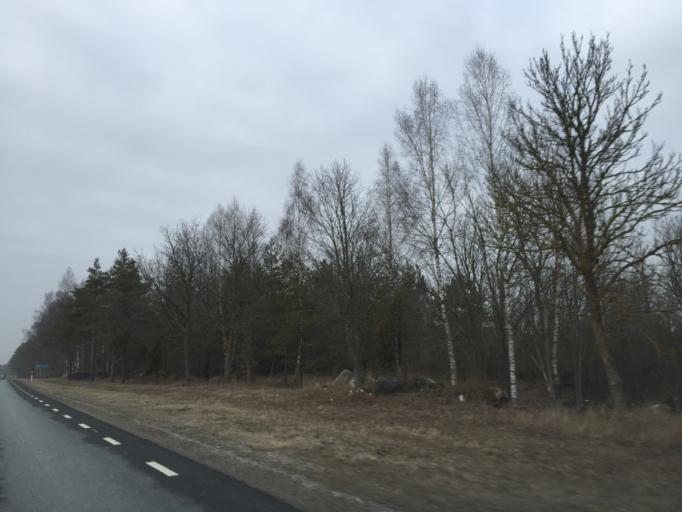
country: EE
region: Saare
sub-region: Orissaare vald
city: Orissaare
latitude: 58.5927
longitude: 23.3317
